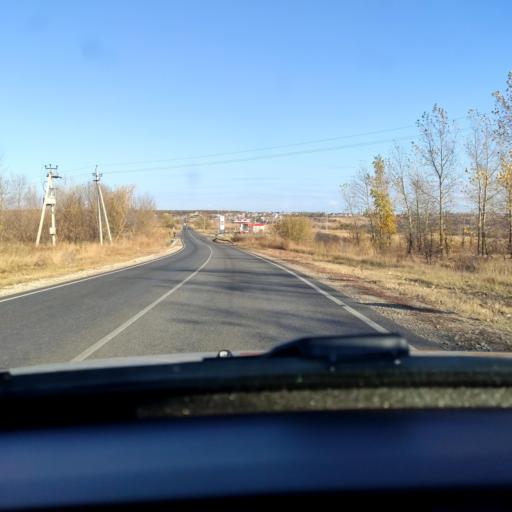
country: RU
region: Voronezj
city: Semiluki
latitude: 51.7231
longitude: 38.9973
